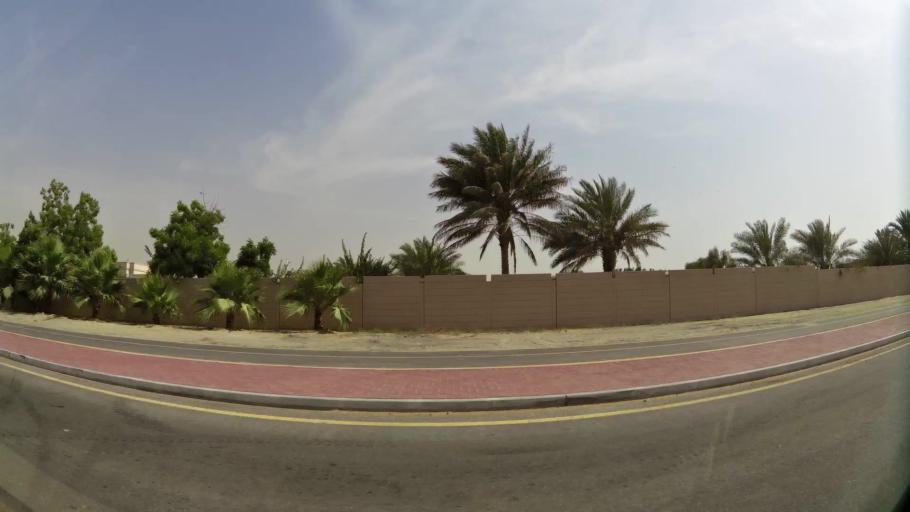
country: AE
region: Ash Shariqah
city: Sharjah
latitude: 25.2433
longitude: 55.4818
